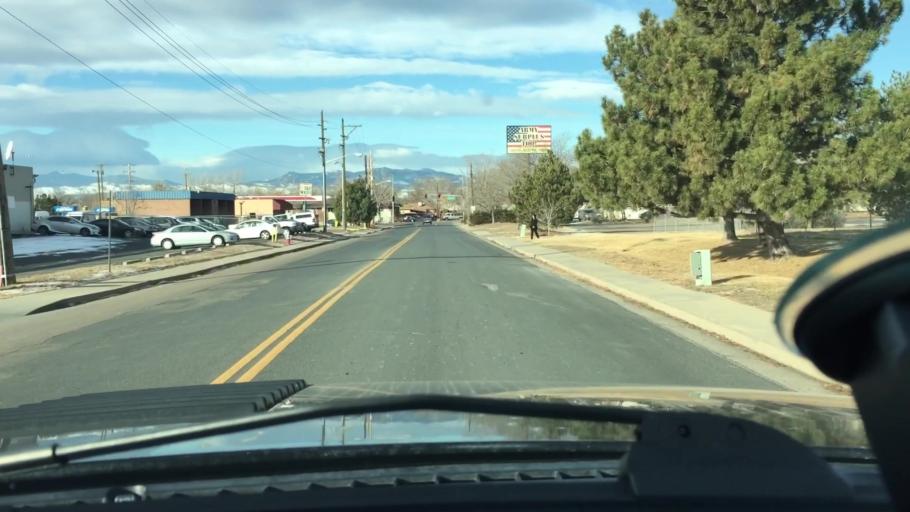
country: US
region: Colorado
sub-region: Adams County
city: Sherrelwood
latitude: 39.8325
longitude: -105.0037
